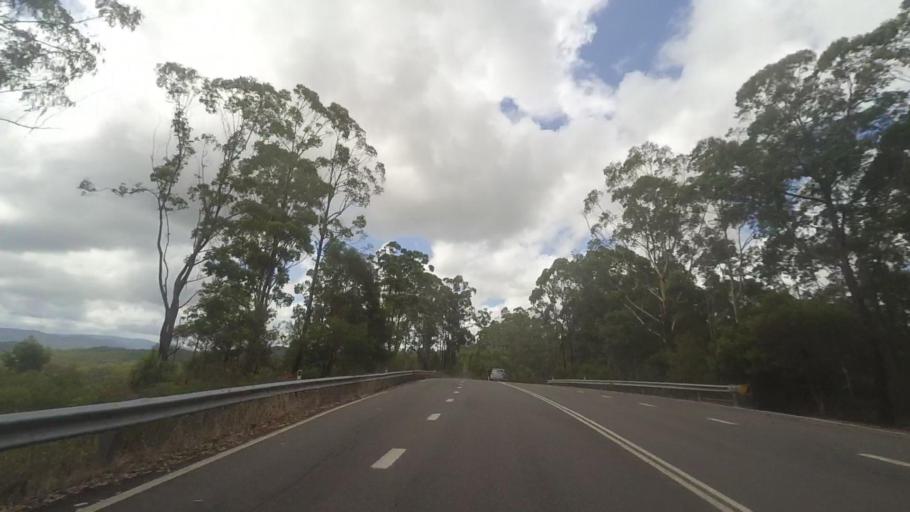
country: AU
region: New South Wales
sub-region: Great Lakes
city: Bulahdelah
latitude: -32.3926
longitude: 152.2468
